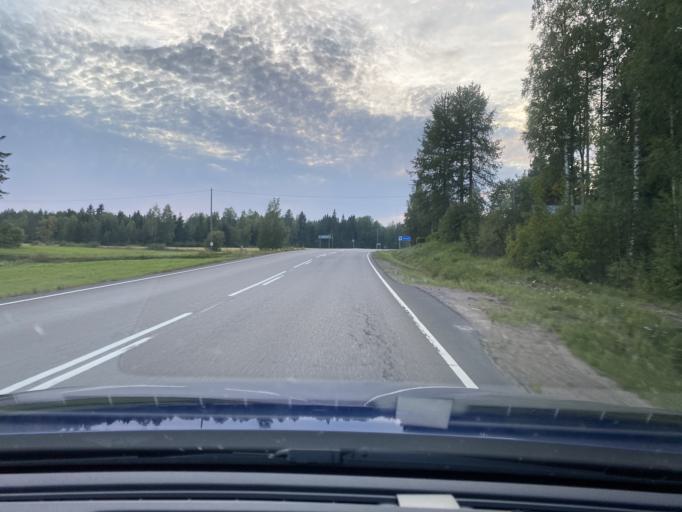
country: FI
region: Satakunta
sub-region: Pohjois-Satakunta
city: Honkajoki
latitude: 61.9207
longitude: 22.2553
